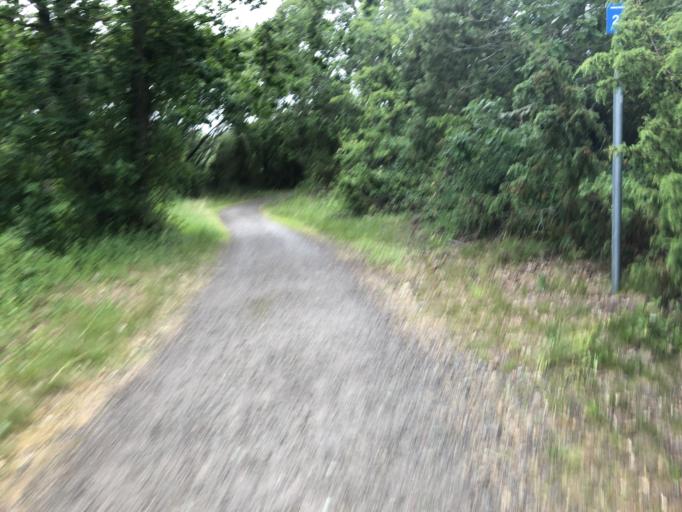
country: SE
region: Kalmar
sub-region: Kalmar Kommun
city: Kalmar
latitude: 56.6365
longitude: 16.3214
